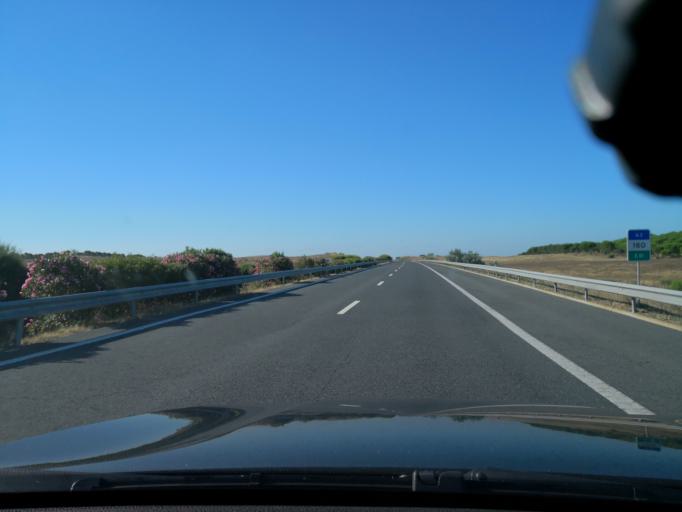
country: PT
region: Beja
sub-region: Aljustrel
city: Aljustrel
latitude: 37.8162
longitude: -8.2309
